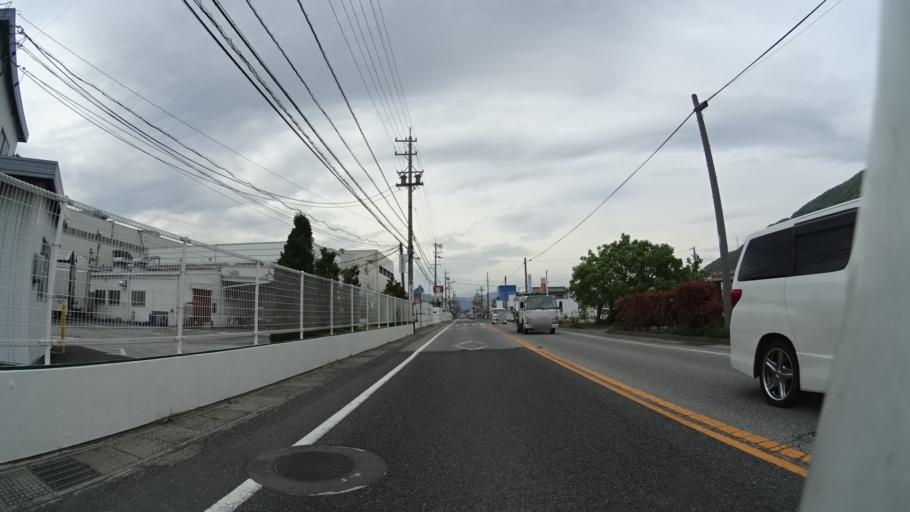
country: JP
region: Nagano
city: Nagano-shi
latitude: 36.5158
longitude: 138.1325
